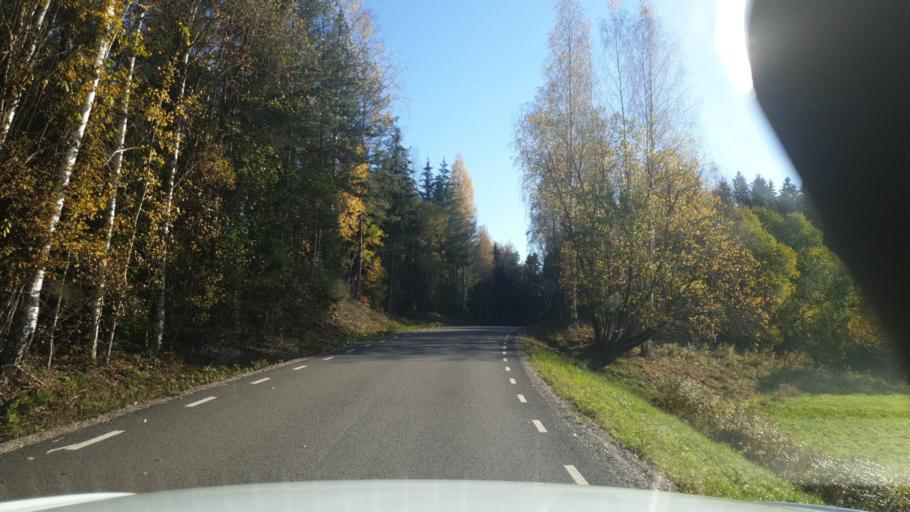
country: SE
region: Vaermland
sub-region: Arvika Kommun
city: Arvika
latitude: 59.6394
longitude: 12.8160
